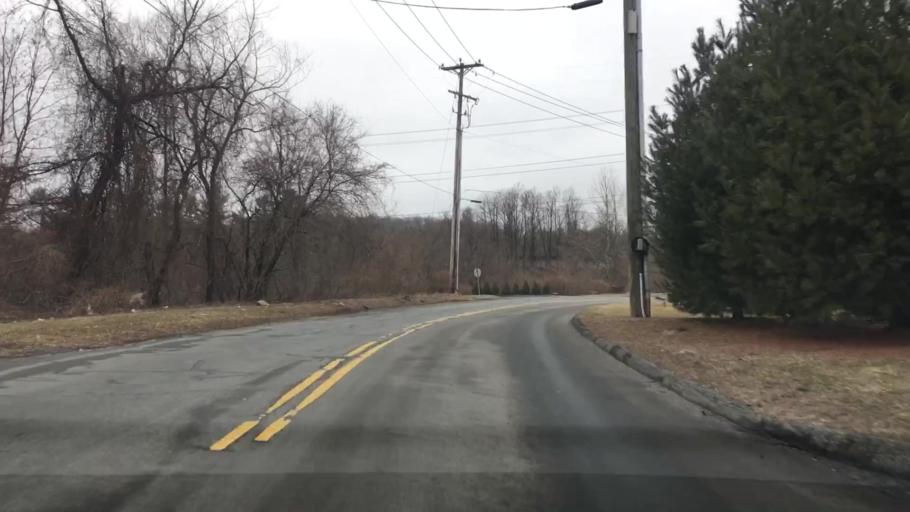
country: US
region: Connecticut
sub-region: Fairfield County
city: Bethel
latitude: 41.4379
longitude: -73.3979
